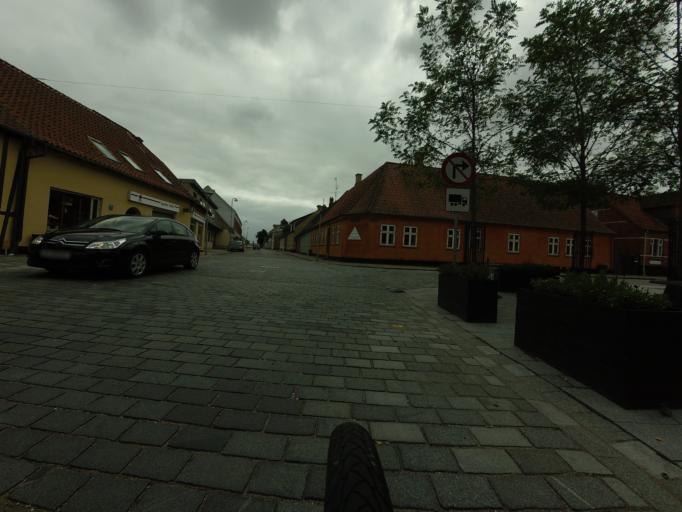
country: DK
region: Zealand
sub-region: Stevns Kommune
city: Store Heddinge
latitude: 55.3089
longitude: 12.3888
